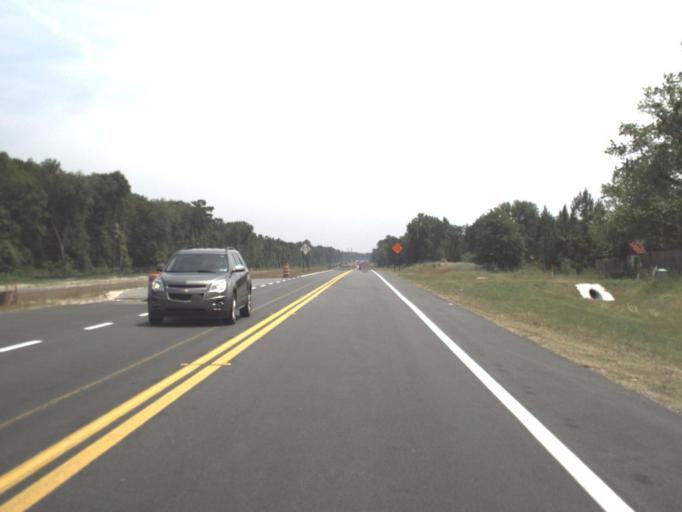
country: US
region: Florida
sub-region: Nassau County
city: Callahan
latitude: 30.5315
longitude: -81.8592
